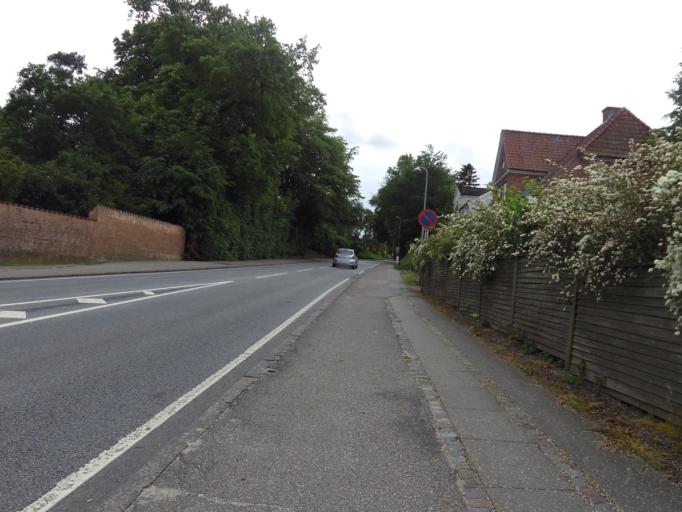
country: DK
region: South Denmark
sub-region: Haderslev Kommune
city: Gram
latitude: 55.2936
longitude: 9.0541
